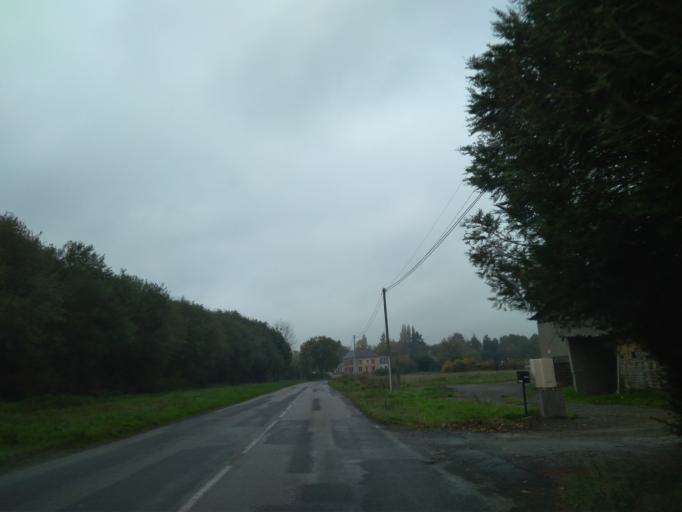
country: FR
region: Brittany
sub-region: Departement d'Ille-et-Vilaine
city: Saint-Gregoire
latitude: 48.1494
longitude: -1.6760
